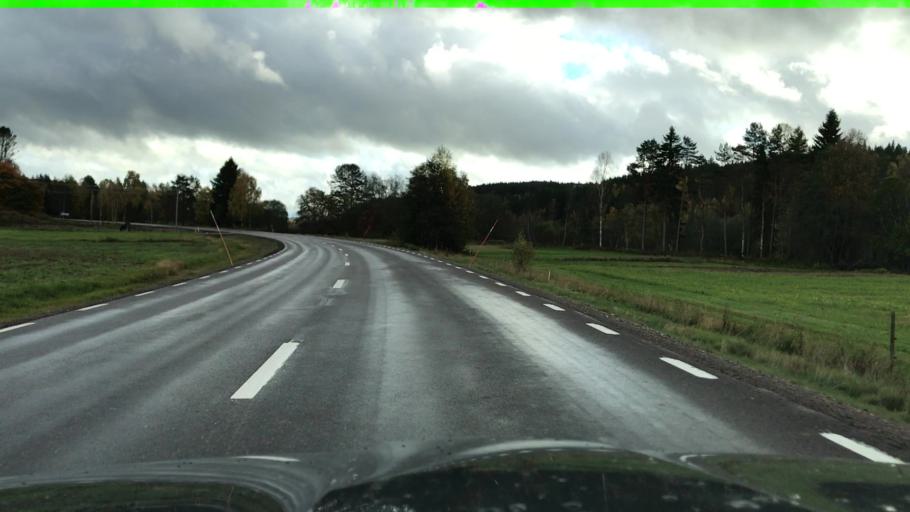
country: SE
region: Vaermland
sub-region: Hagfors Kommun
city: Ekshaerad
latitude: 60.4324
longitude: 13.2383
